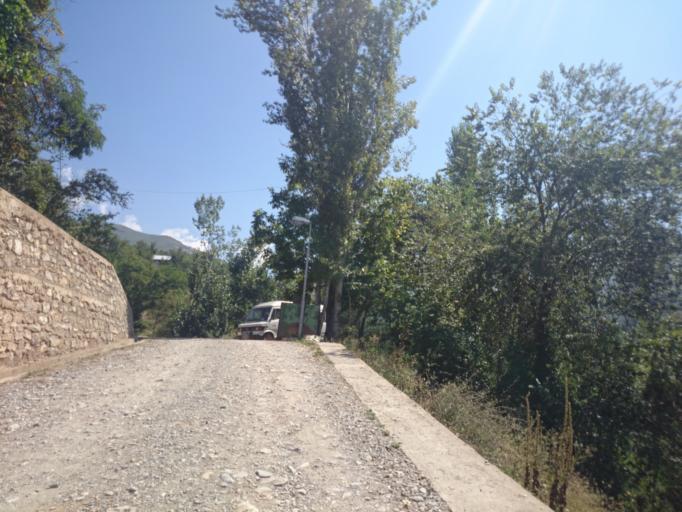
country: AL
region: Diber
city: Peshkopi
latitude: 41.6861
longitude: 20.4361
